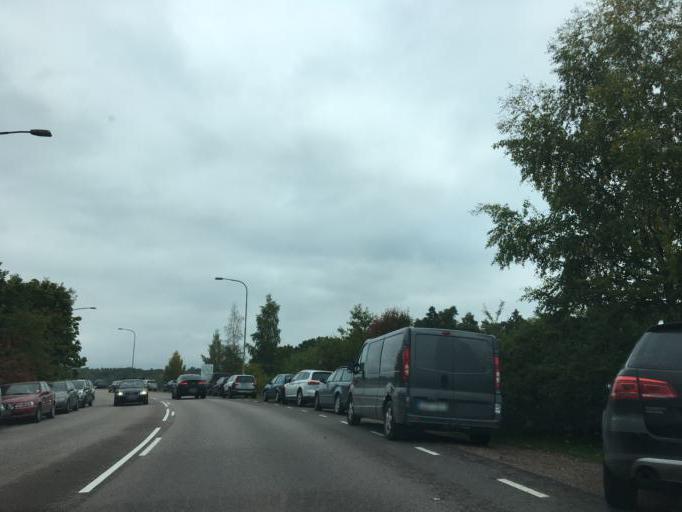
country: SE
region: Vaestmanland
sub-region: Vasteras
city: Vasteras
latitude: 59.6210
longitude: 16.5128
